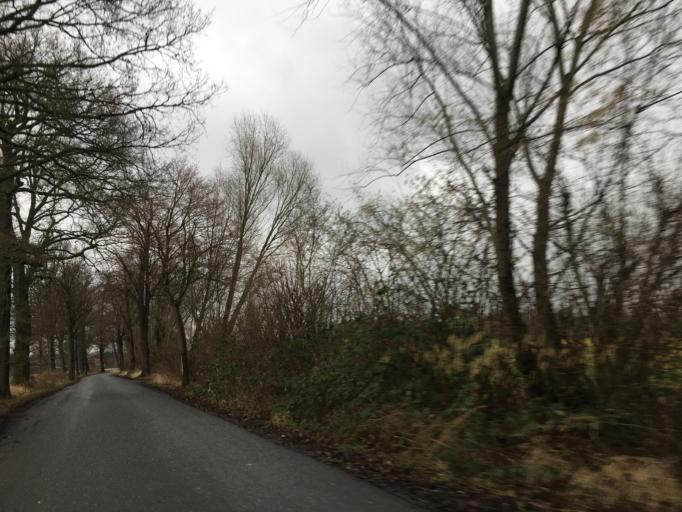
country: DE
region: North Rhine-Westphalia
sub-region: Regierungsbezirk Munster
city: Nordwalde
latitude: 52.0943
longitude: 7.5009
